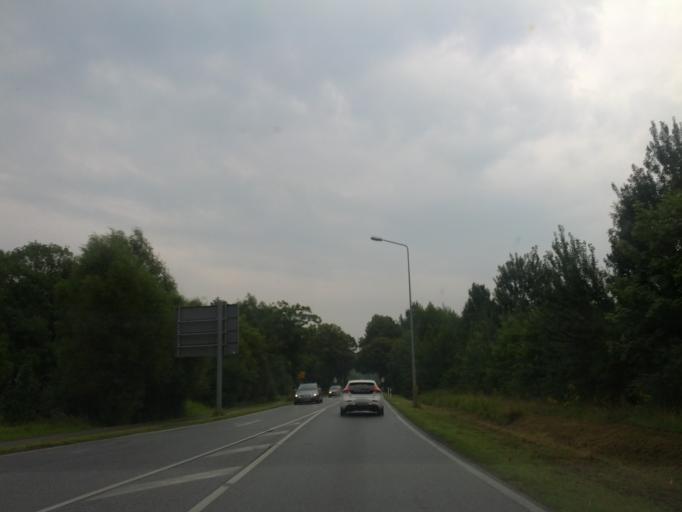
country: DE
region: Mecklenburg-Vorpommern
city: Bad Doberan
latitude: 54.1065
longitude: 11.9303
